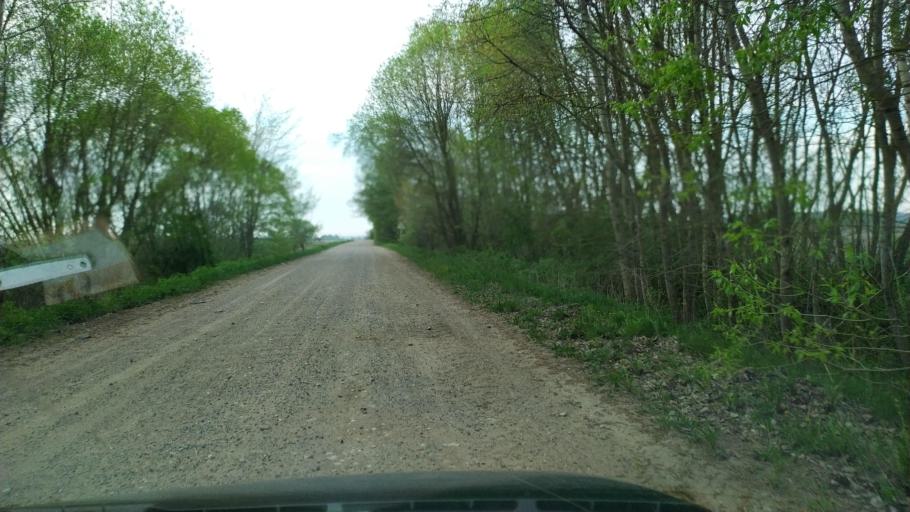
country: BY
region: Brest
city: Zhabinka
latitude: 52.1382
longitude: 24.0906
